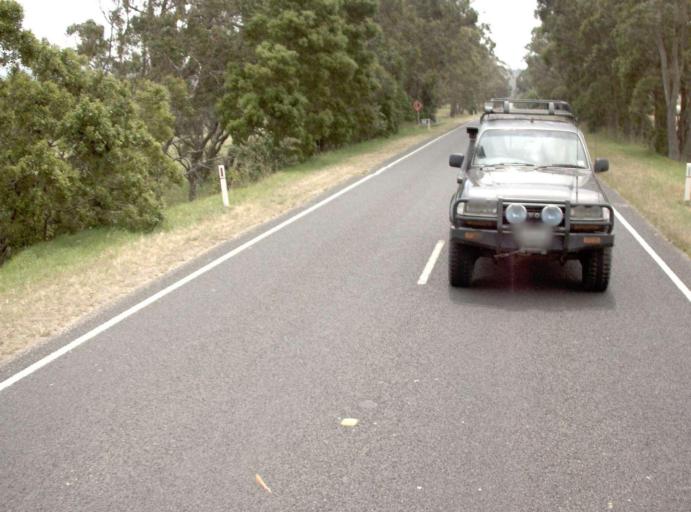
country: AU
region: Victoria
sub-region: Latrobe
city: Traralgon
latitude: -38.4765
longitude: 146.7163
